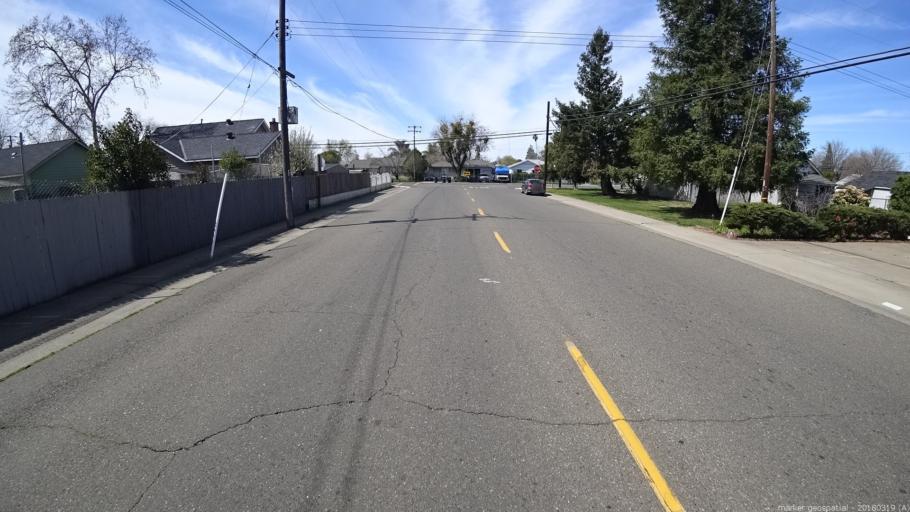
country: US
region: California
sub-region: Sacramento County
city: Parkway
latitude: 38.5138
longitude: -121.4482
